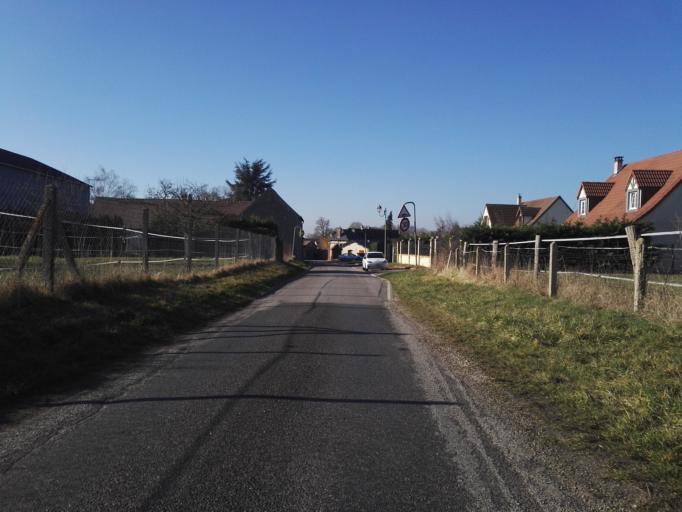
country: FR
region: Haute-Normandie
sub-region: Departement de l'Eure
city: Pacy-sur-Eure
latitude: 49.0087
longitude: 1.4218
